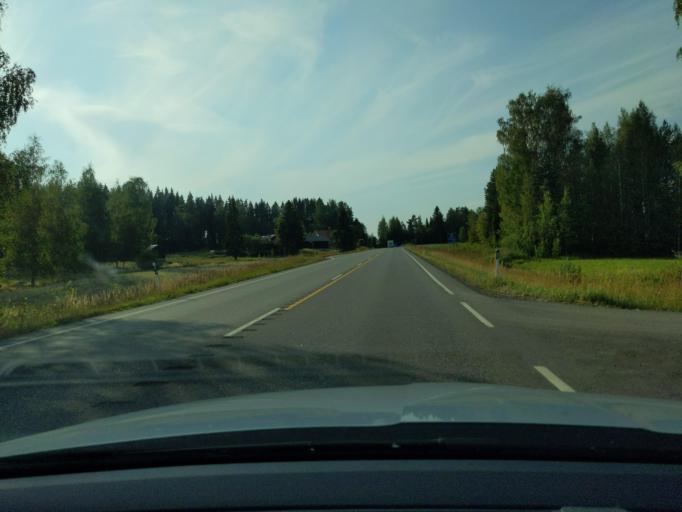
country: FI
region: Paijanne Tavastia
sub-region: Lahti
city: Padasjoki
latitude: 61.3390
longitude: 25.2596
